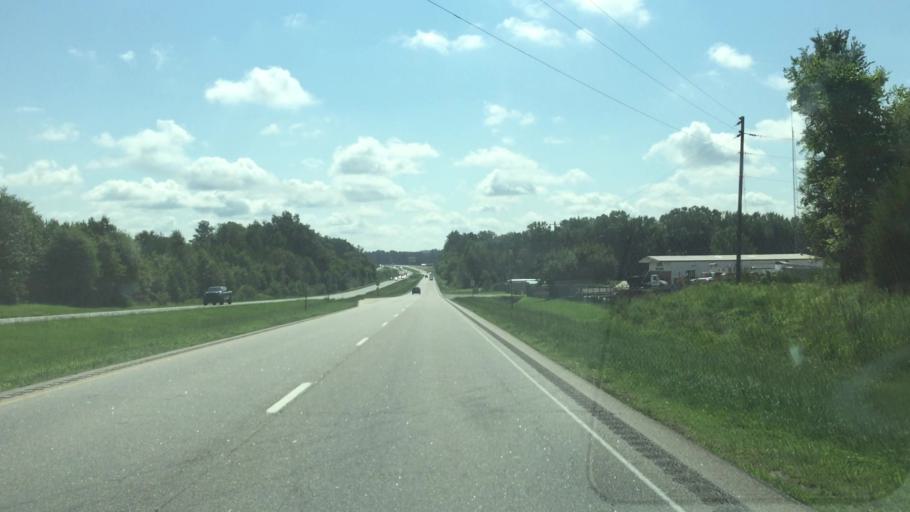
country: US
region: North Carolina
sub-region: Anson County
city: Wadesboro
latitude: 34.9816
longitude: -80.1313
